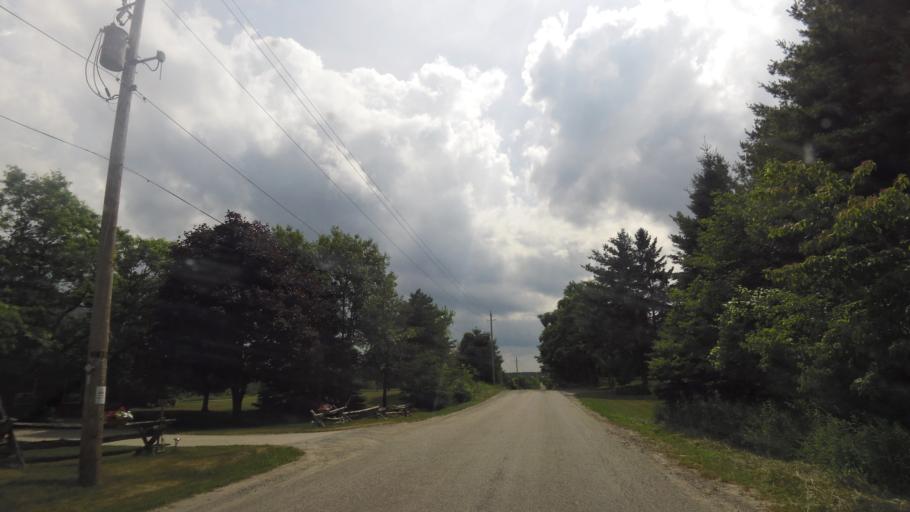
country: CA
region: Ontario
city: Orangeville
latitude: 43.8783
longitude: -79.9265
